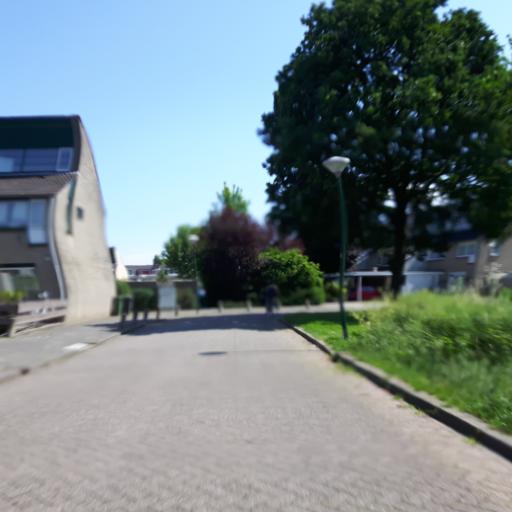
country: NL
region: Utrecht
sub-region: Stichtse Vecht
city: Spechtenkamp
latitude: 52.1254
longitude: 5.0282
